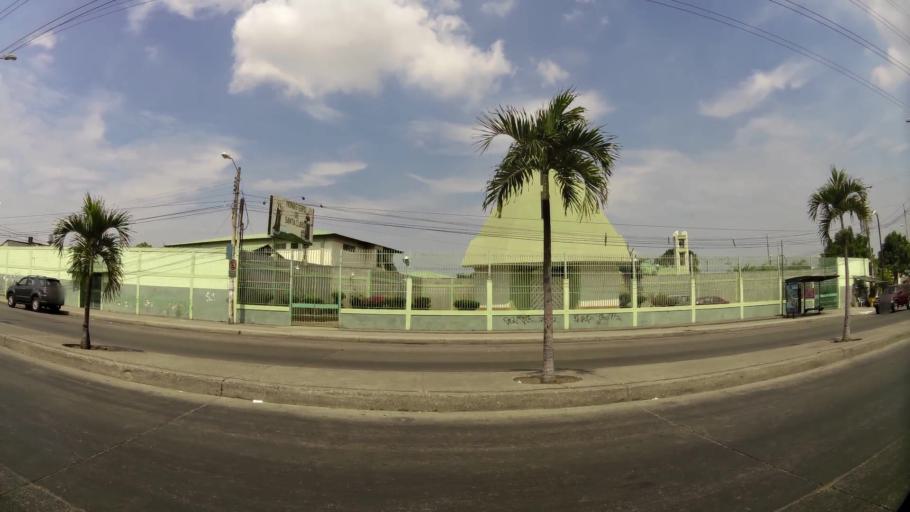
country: EC
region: Guayas
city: Guayaquil
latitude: -2.2586
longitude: -79.8890
